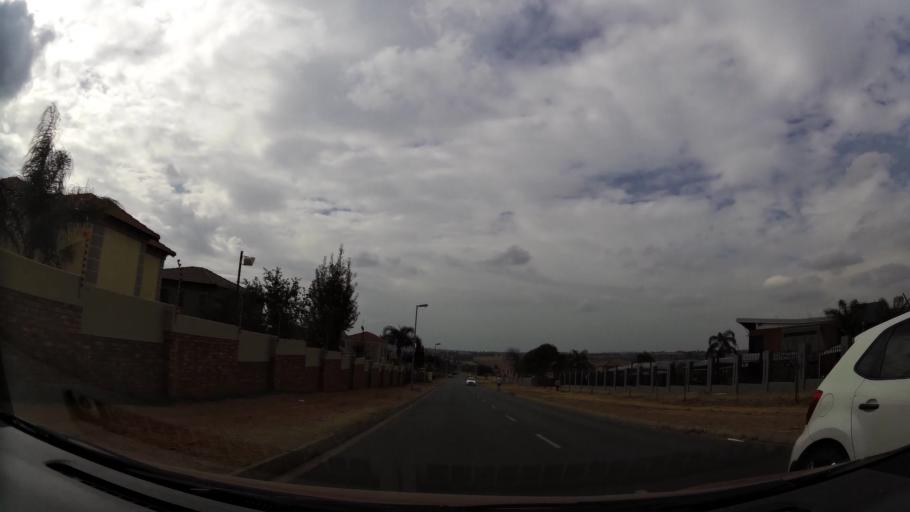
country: ZA
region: Gauteng
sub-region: City of Johannesburg Metropolitan Municipality
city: Roodepoort
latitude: -26.0974
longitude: 27.8757
